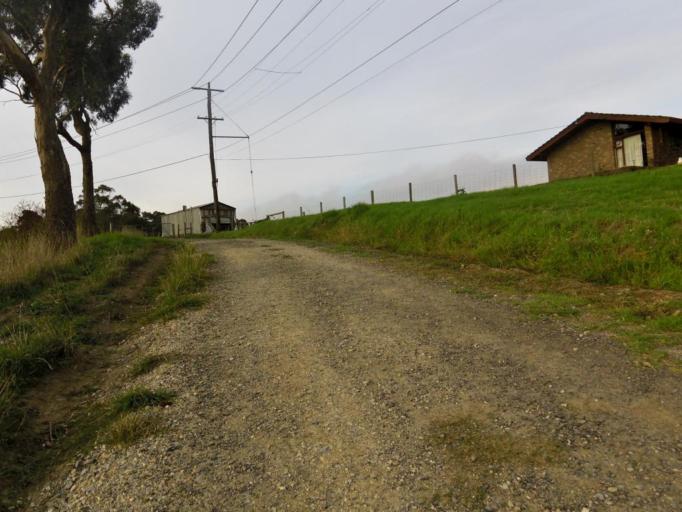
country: AU
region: Victoria
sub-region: Yarra Ranges
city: Belgrave South
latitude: -37.9212
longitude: 145.3250
